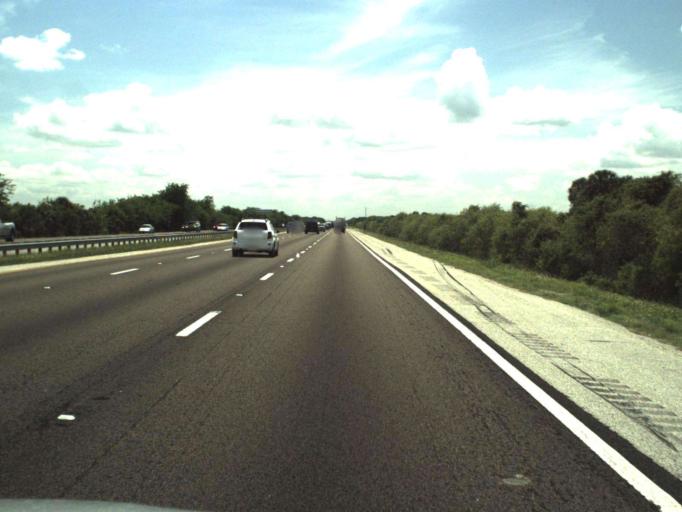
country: US
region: Florida
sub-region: Volusia County
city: DeBary
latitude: 28.8621
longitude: -81.2928
